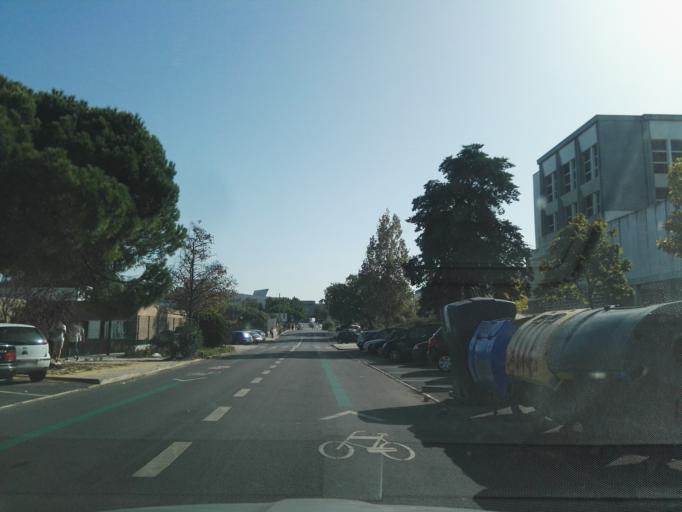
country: PT
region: Lisbon
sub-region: Odivelas
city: Olival do Basto
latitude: 38.7520
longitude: -9.1559
